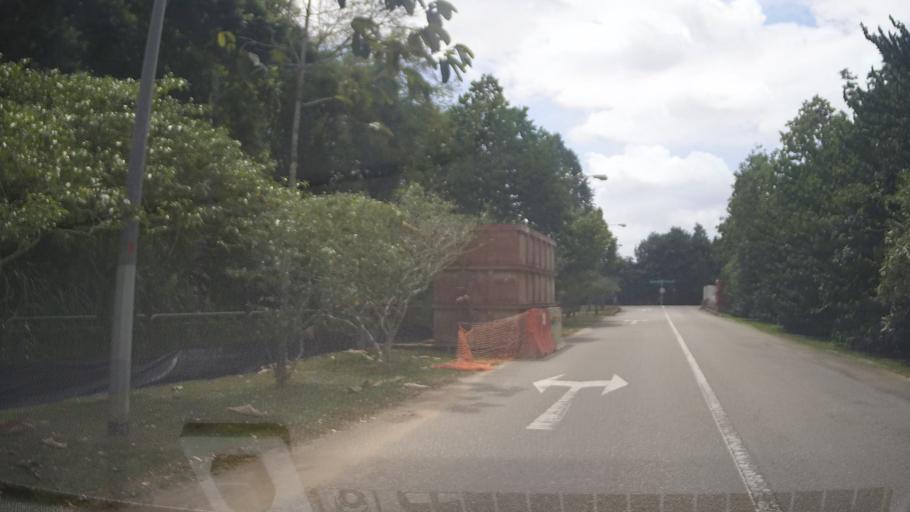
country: MY
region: Johor
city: Johor Bahru
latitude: 1.4395
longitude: 103.7321
